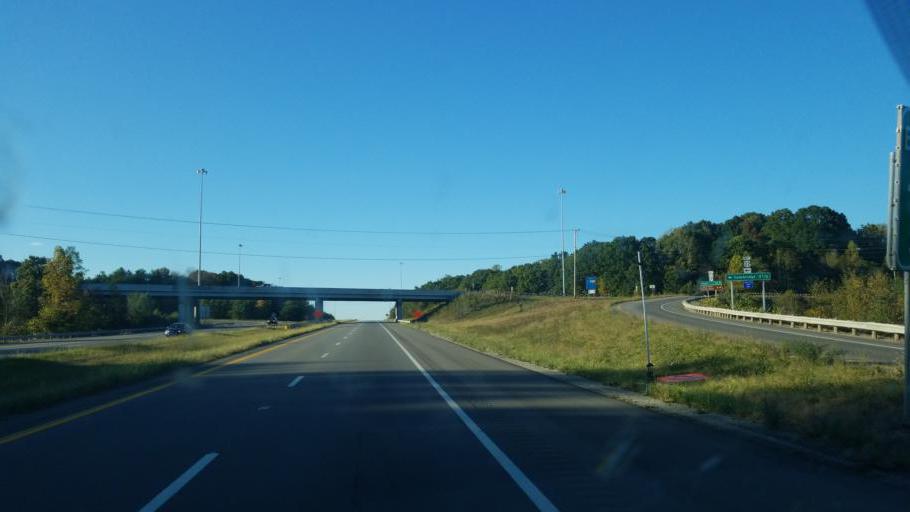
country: US
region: Ohio
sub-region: Guernsey County
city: Cambridge
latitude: 40.0482
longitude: -81.5625
